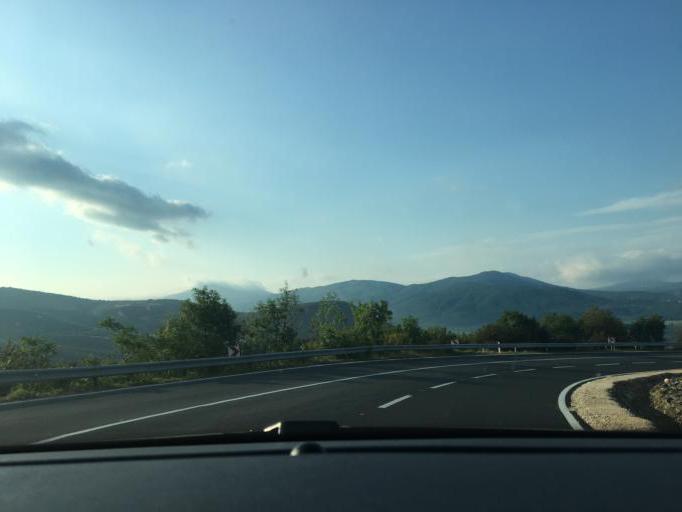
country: MK
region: Valandovo
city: Valandovo
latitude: 41.3237
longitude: 22.5976
